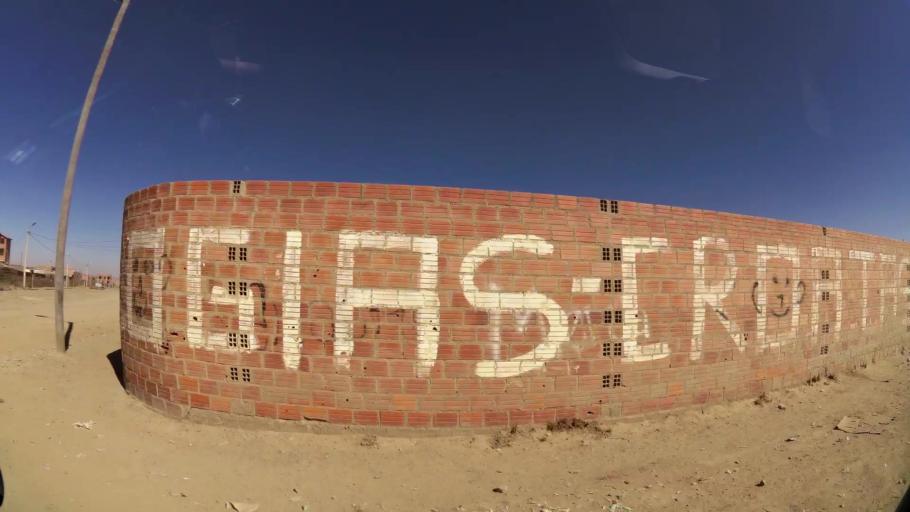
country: BO
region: La Paz
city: La Paz
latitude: -16.6191
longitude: -68.1837
